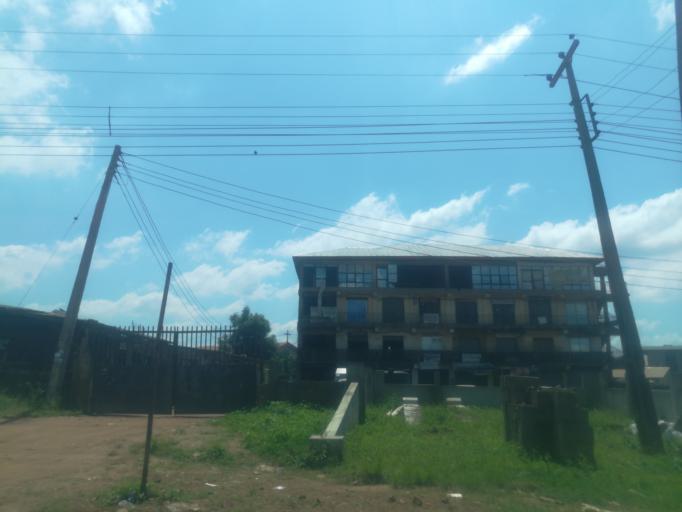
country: NG
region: Oyo
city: Ibadan
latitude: 7.3534
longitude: 3.8638
